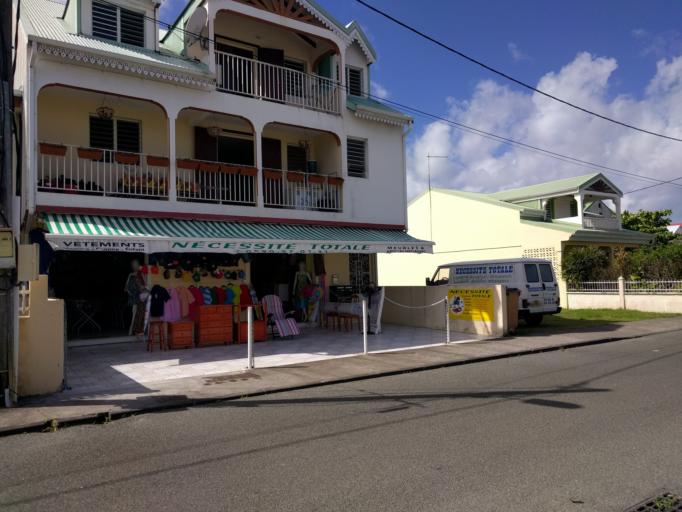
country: GP
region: Guadeloupe
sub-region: Guadeloupe
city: Grand-Bourg
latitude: 15.9537
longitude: -61.3164
